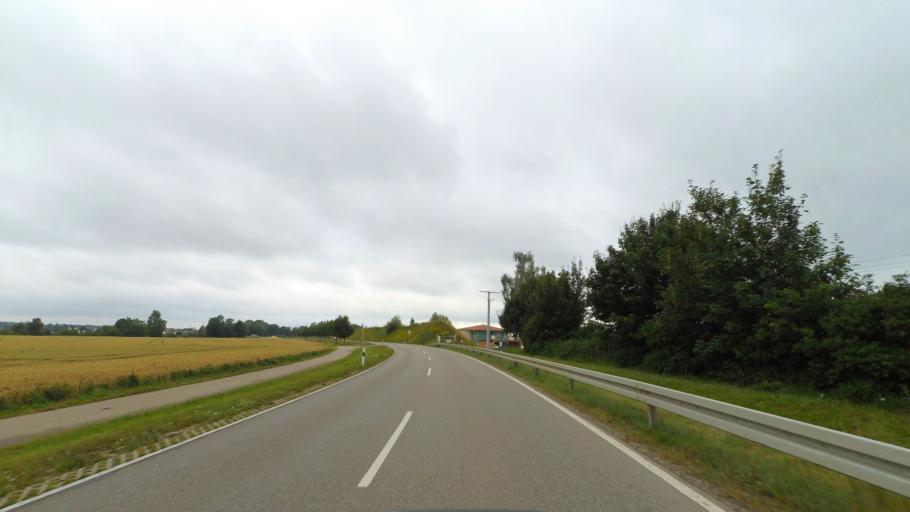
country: DE
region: Bavaria
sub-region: Swabia
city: Leipheim
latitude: 48.4632
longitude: 10.2033
